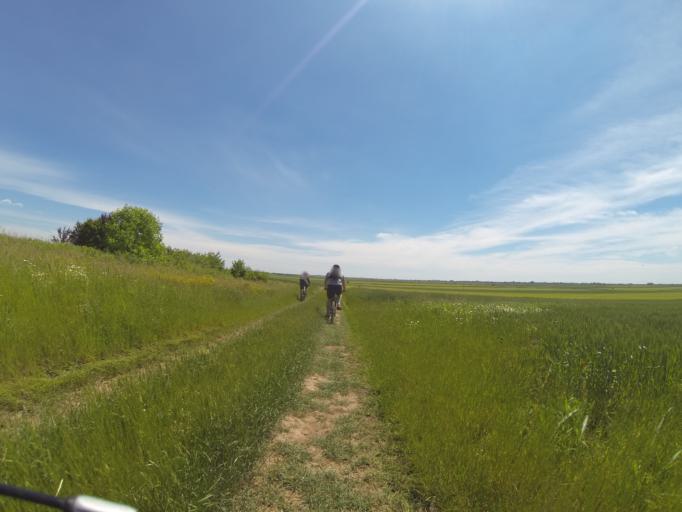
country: RO
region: Dolj
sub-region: Comuna Leu
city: Zanoaga
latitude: 44.1806
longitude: 24.0775
